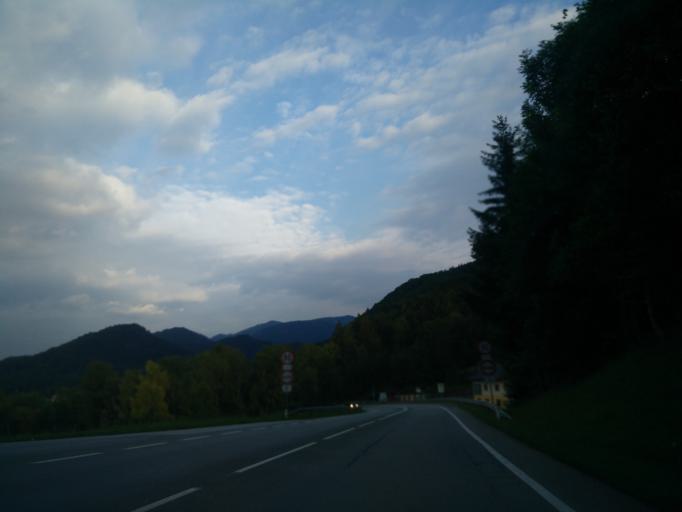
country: AT
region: Salzburg
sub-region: Politischer Bezirk Salzburg-Umgebung
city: Fuschl am See
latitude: 47.7942
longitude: 13.2828
